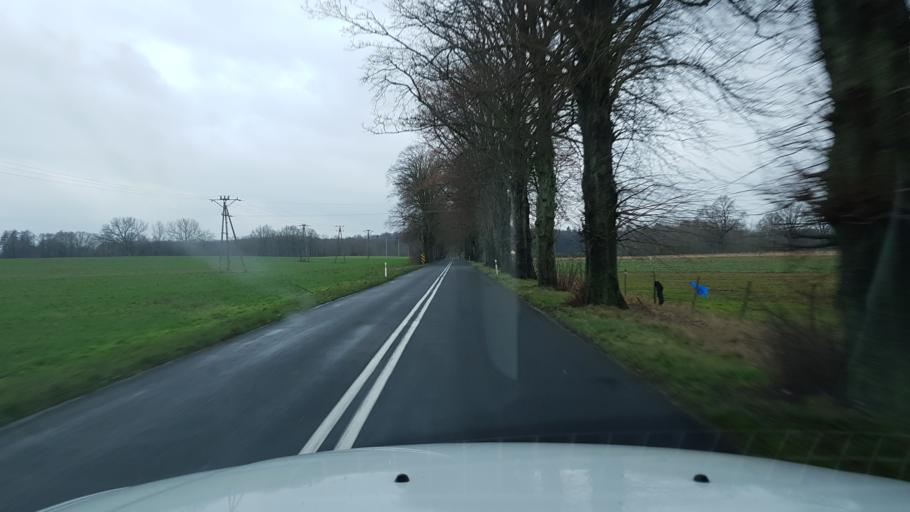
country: PL
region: West Pomeranian Voivodeship
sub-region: Powiat gryficki
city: Brojce
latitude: 54.0577
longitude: 15.3713
